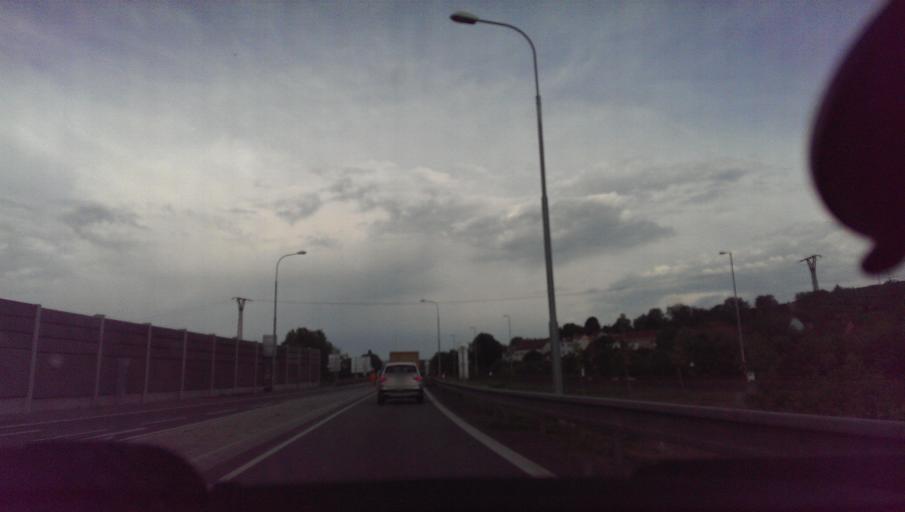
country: CZ
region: South Moravian
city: Nesovice
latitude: 49.1499
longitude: 17.0835
